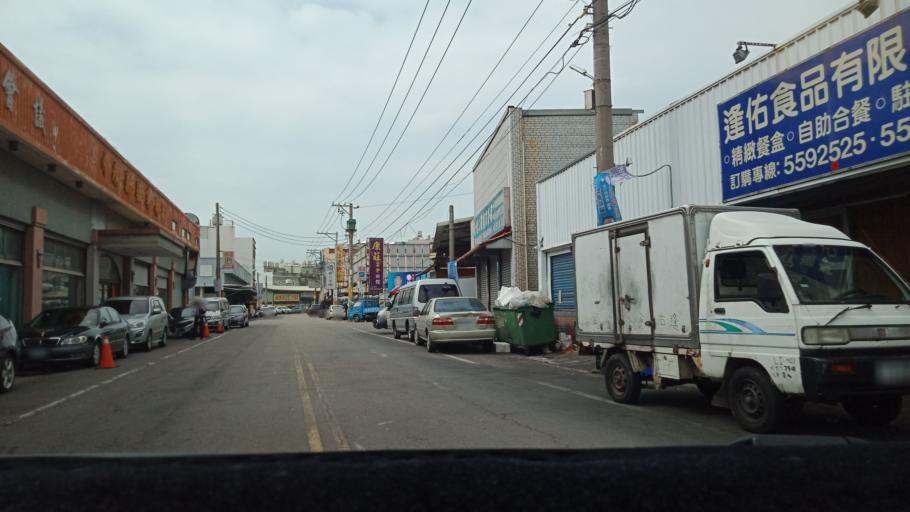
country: TW
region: Taiwan
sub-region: Hsinchu
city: Zhubei
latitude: 24.8734
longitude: 120.9981
